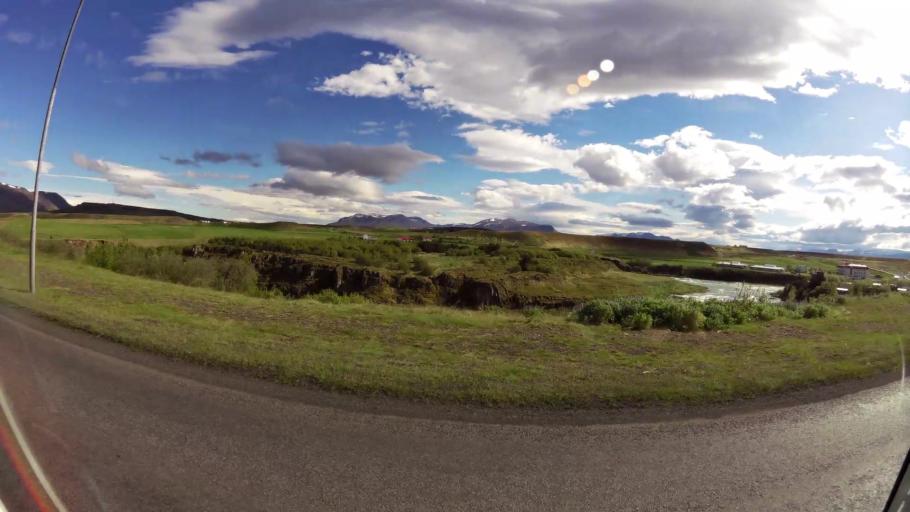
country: IS
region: Northwest
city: Saudarkrokur
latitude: 65.6602
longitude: -20.2715
